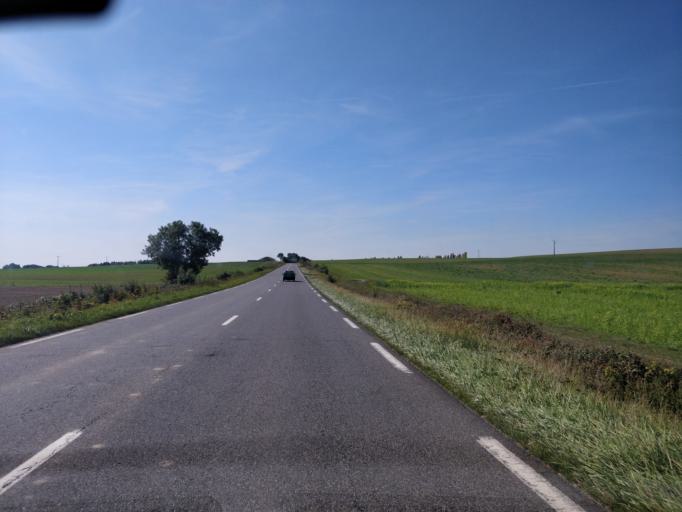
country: FR
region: Champagne-Ardenne
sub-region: Departement de l'Aube
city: Bouilly
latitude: 48.1547
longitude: 4.0188
